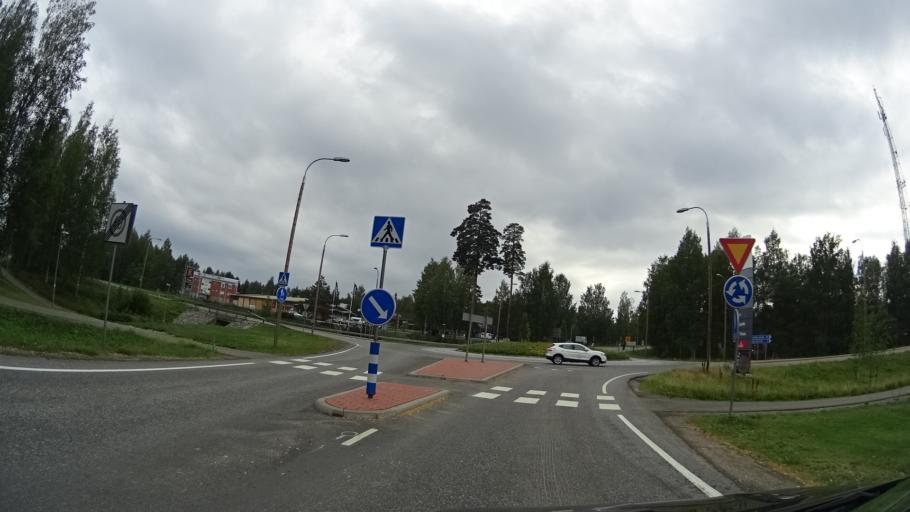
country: FI
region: Southern Savonia
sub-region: Savonlinna
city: Punkaharju
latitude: 61.7562
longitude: 29.3938
